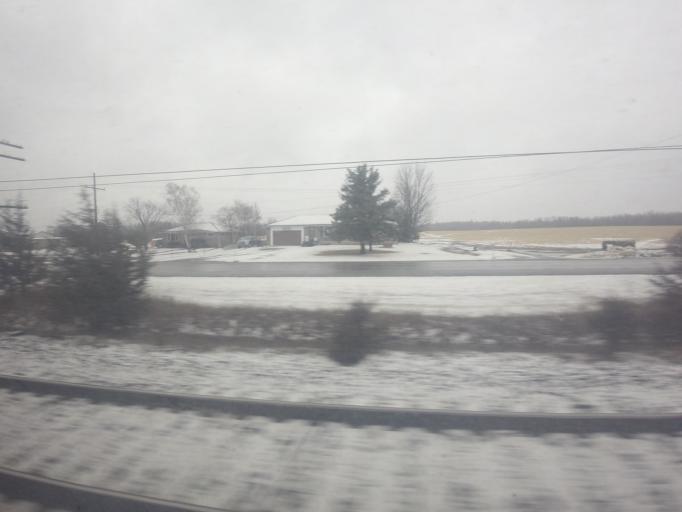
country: CA
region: Ontario
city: Belleville
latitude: 44.1589
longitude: -77.4474
